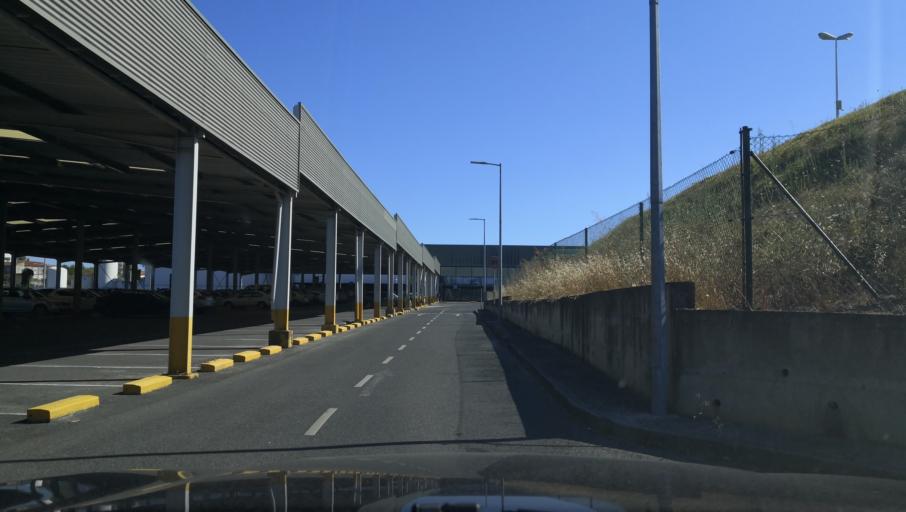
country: PT
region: Santarem
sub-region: Santarem
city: Santarem
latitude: 39.2372
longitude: -8.7043
